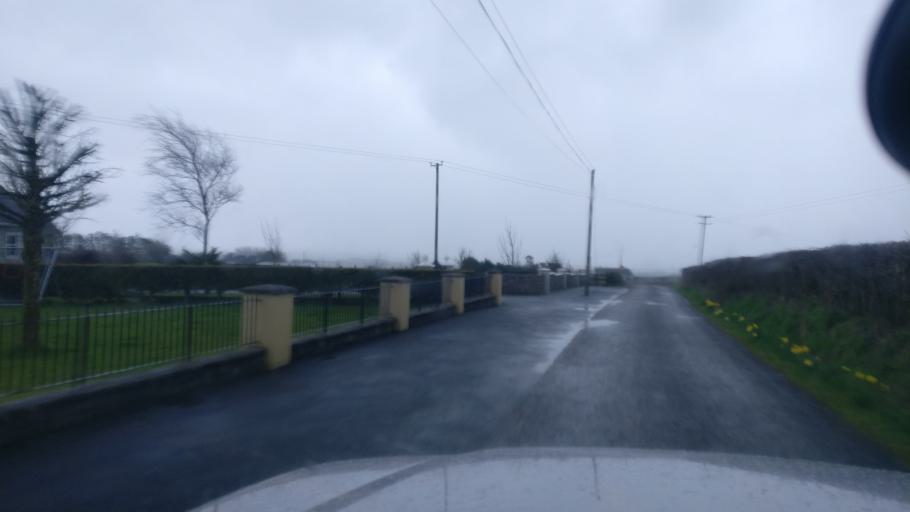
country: IE
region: Connaught
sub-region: County Galway
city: Loughrea
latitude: 53.2299
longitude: -8.4258
